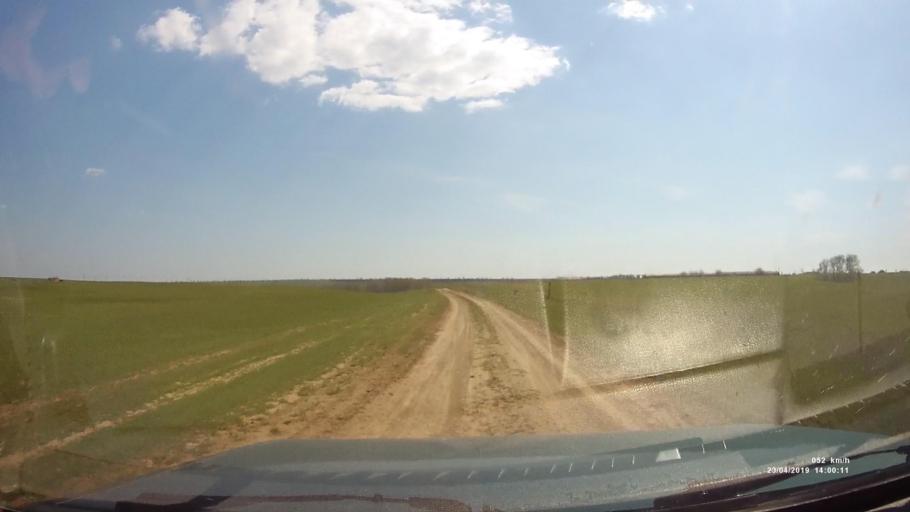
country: RU
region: Rostov
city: Remontnoye
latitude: 46.5611
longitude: 42.9470
